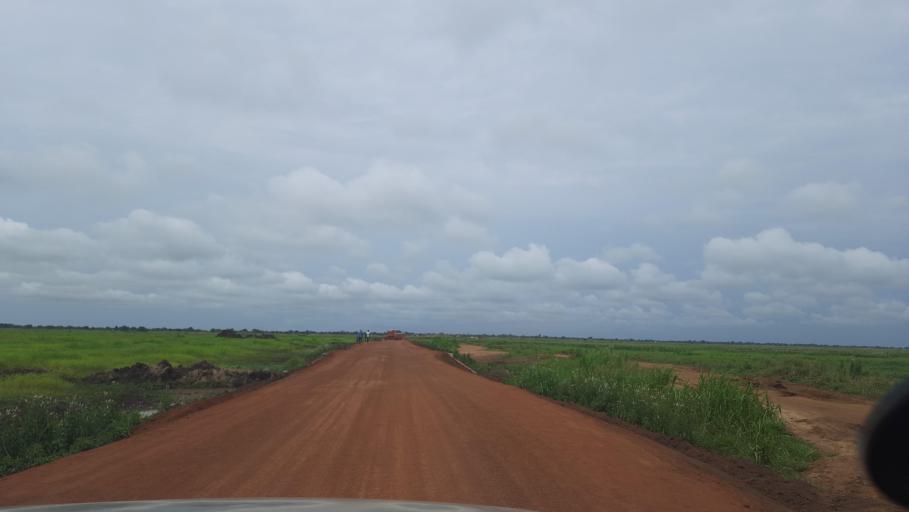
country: ET
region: Gambela
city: Gambela
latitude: 8.3455
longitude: 33.7812
